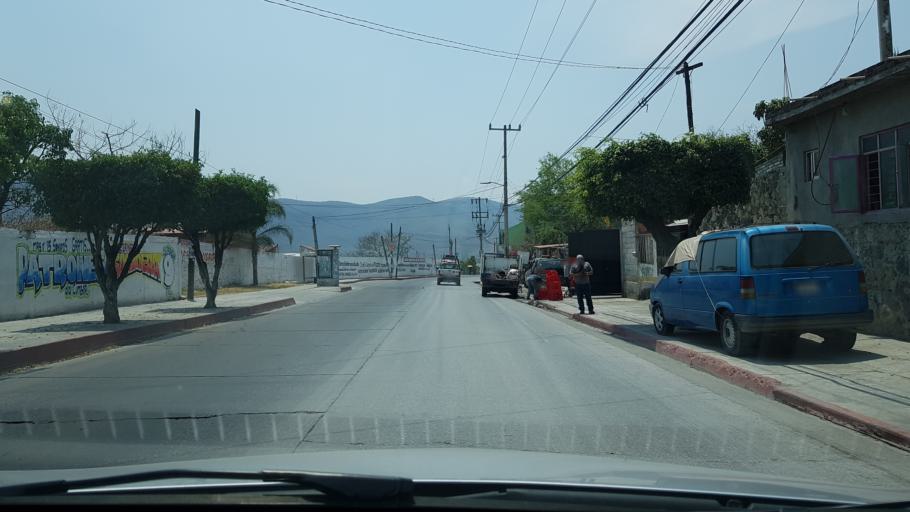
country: MX
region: Morelos
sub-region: Jiutepec
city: Calera Chica
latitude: 18.8548
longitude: -99.1791
